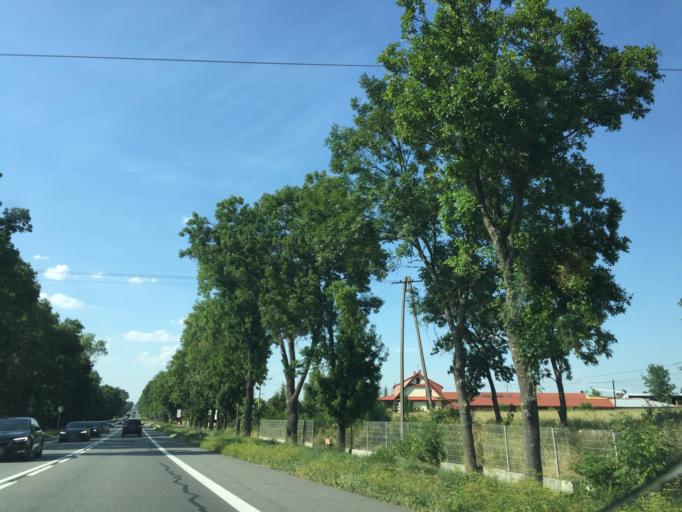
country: PL
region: Lesser Poland Voivodeship
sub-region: Powiat krakowski
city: Slomniki
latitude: 50.2541
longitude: 20.0866
